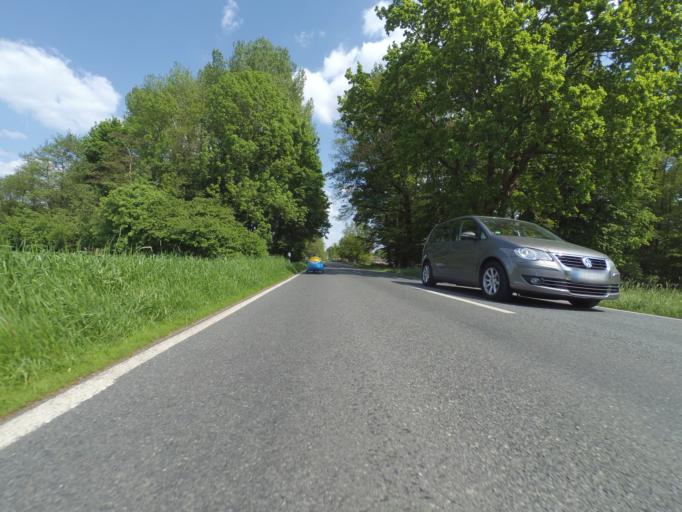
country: DE
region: Lower Saxony
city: Burgdorf
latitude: 52.4635
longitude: 10.0426
